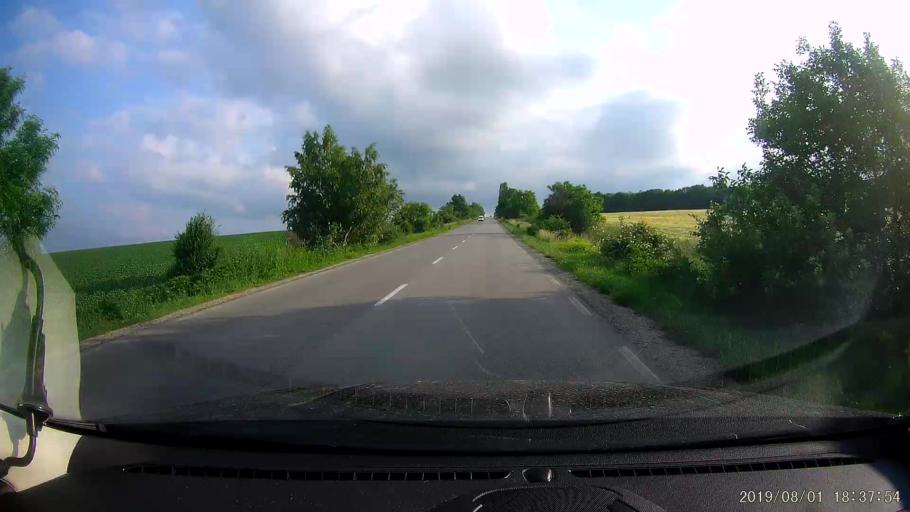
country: BG
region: Shumen
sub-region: Obshtina Khitrino
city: Gara Khitrino
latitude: 43.4117
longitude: 26.9238
